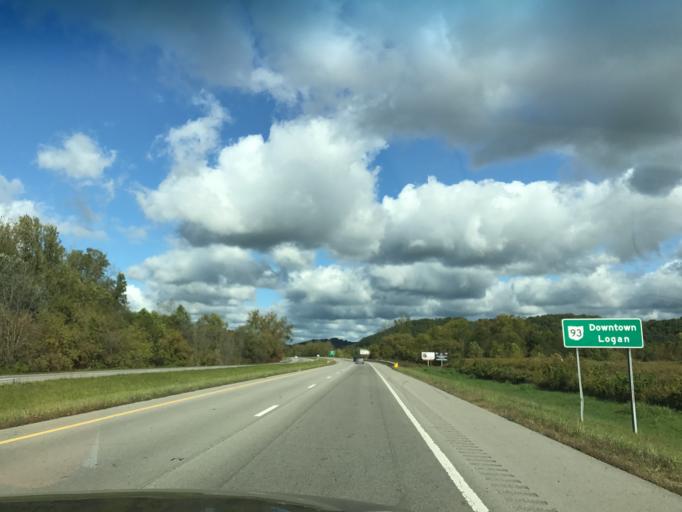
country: US
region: Ohio
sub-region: Hocking County
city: Logan
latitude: 39.5064
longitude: -82.3569
